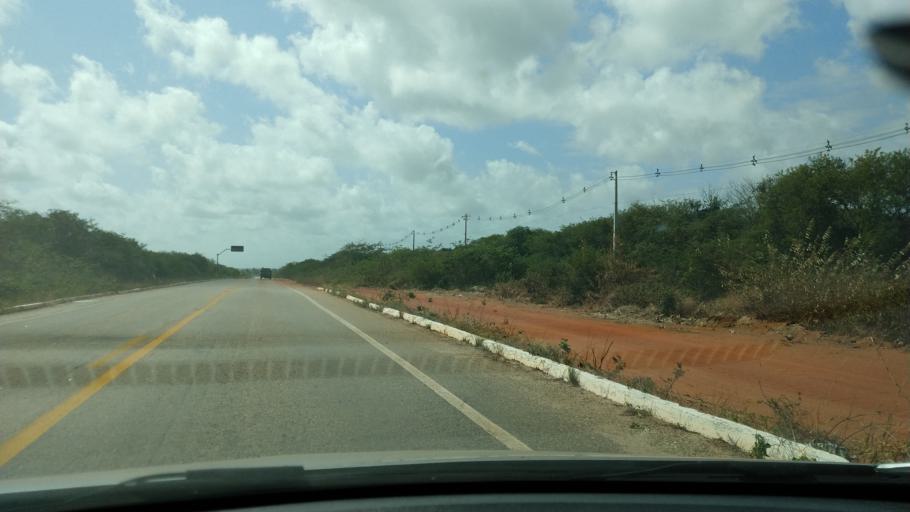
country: BR
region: Rio Grande do Norte
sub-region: Touros
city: Touros
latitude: -5.1954
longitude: -35.5041
